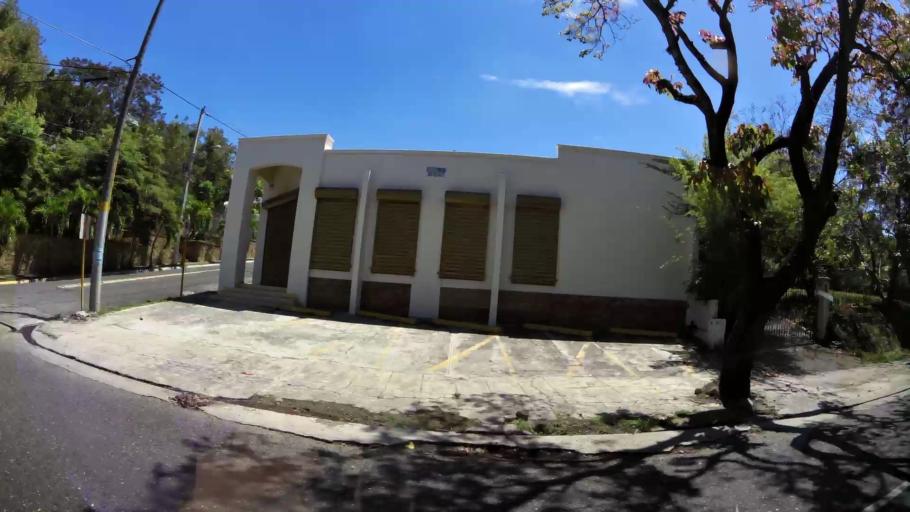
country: DO
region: Santiago
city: Santiago de los Caballeros
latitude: 19.4567
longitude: -70.6931
